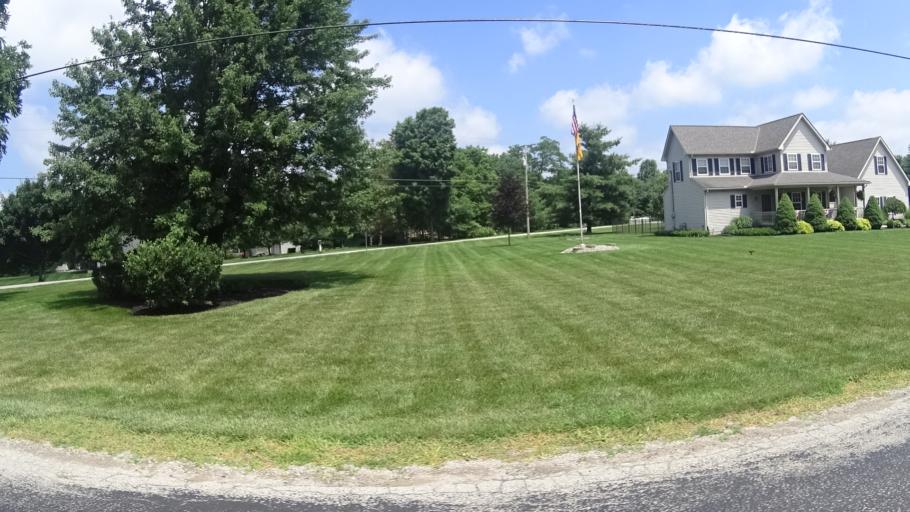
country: US
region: Ohio
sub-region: Huron County
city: Wakeman
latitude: 41.3204
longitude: -82.3507
